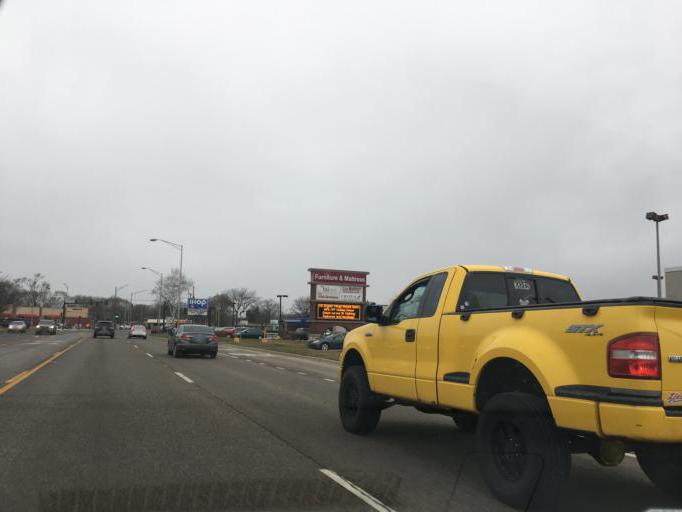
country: US
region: Illinois
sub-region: McHenry County
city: Crystal Lake
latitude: 42.2262
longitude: -88.3249
